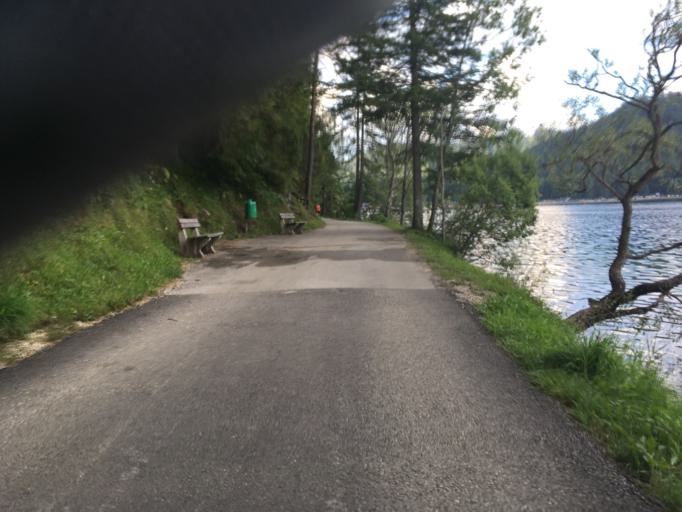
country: AT
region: Lower Austria
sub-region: Politischer Bezirk Lilienfeld
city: Mitterbach am Erlaufsee
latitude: 47.7942
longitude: 15.2739
